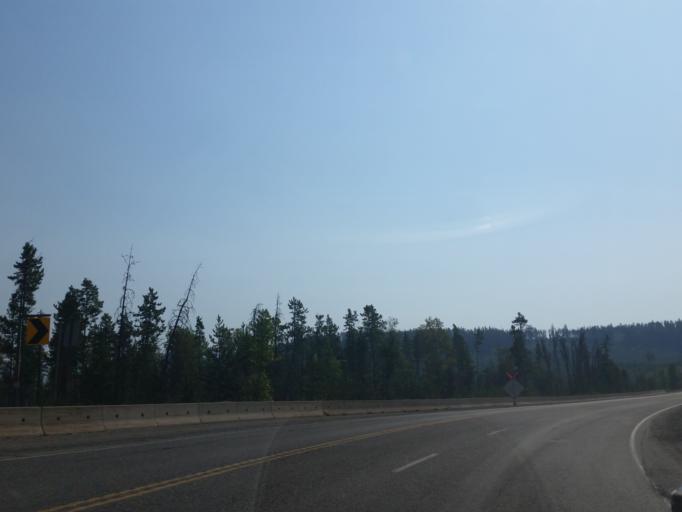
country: CA
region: British Columbia
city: Princeton
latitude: 49.2449
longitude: -120.5718
